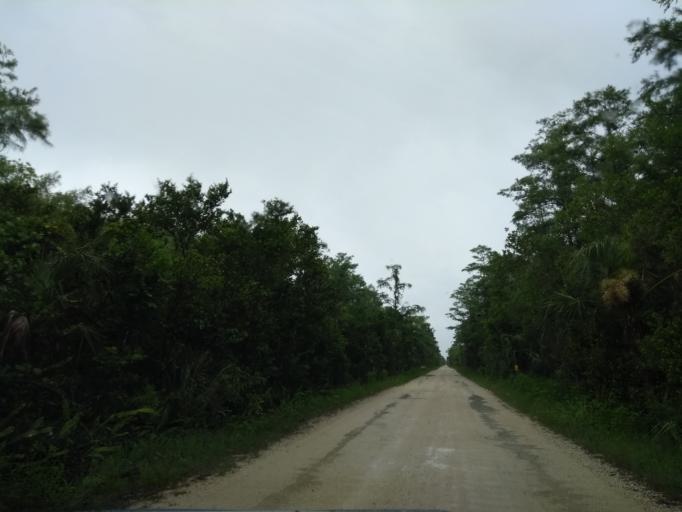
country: US
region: Florida
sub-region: Miami-Dade County
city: The Hammocks
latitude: 25.7602
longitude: -81.0287
